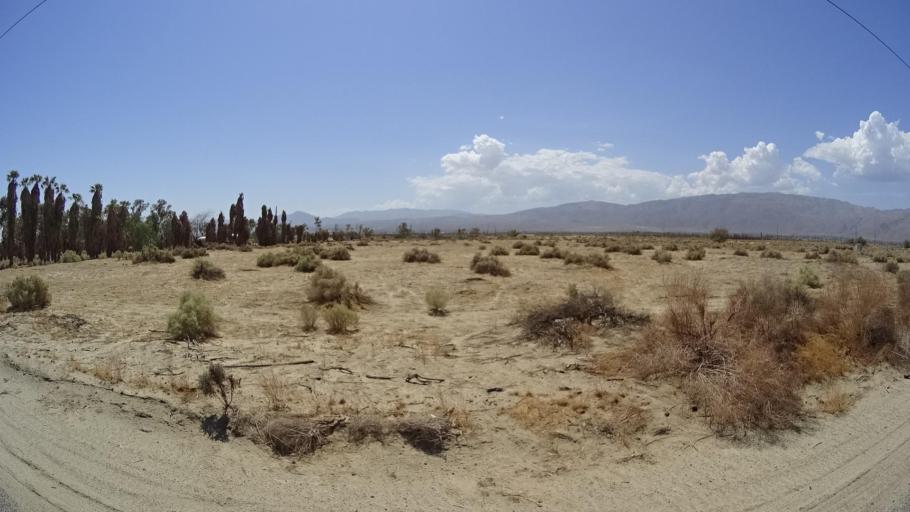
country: US
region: California
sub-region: San Diego County
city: Borrego Springs
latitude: 33.2568
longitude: -116.3431
